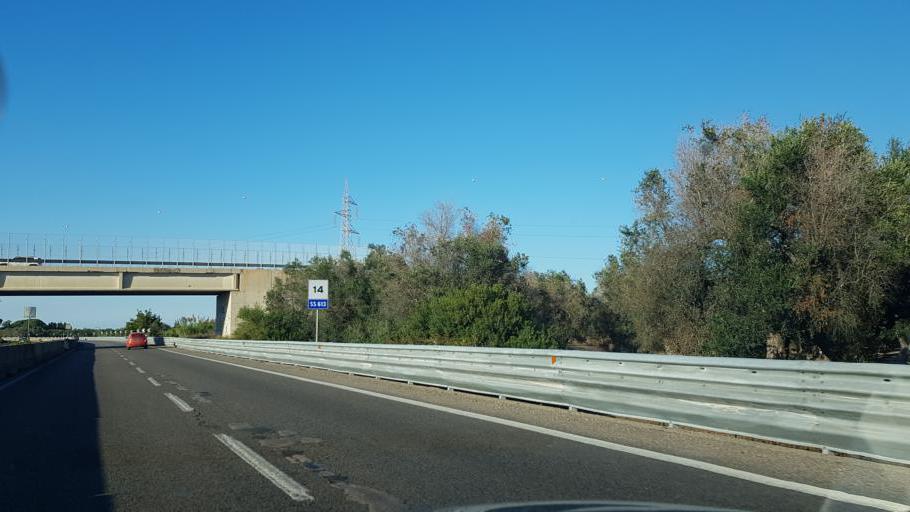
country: IT
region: Apulia
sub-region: Provincia di Brindisi
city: San Pietro Vernotico
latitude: 40.5093
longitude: 18.0241
